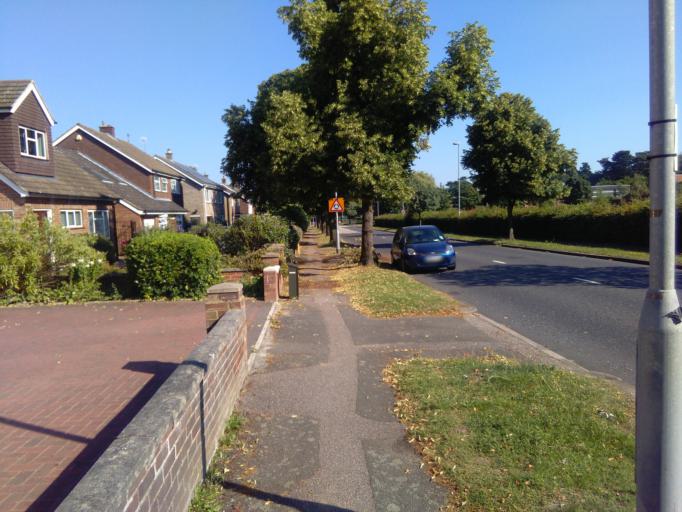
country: GB
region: England
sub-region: Bedford
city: Bedford
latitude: 52.1519
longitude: -0.4604
